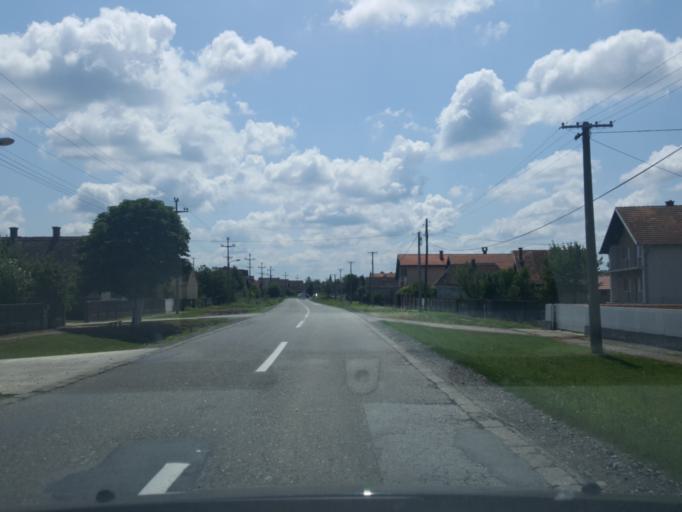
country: RS
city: Metkovic
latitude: 44.8600
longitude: 19.5452
